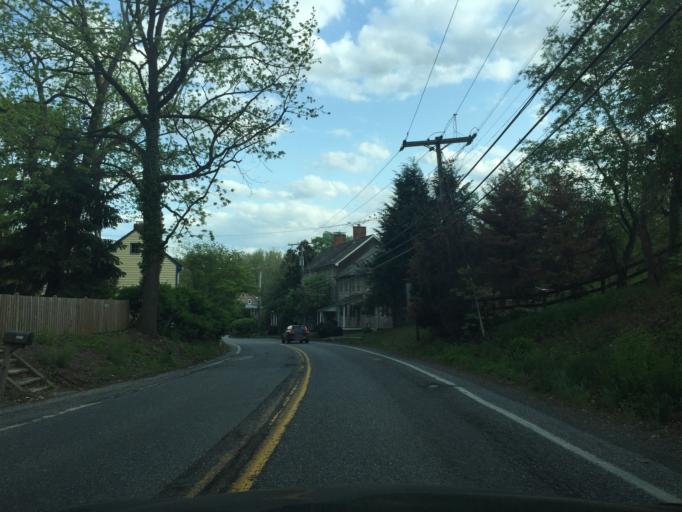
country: US
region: Maryland
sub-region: Baltimore County
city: Mays Chapel
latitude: 39.4013
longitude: -76.6680
